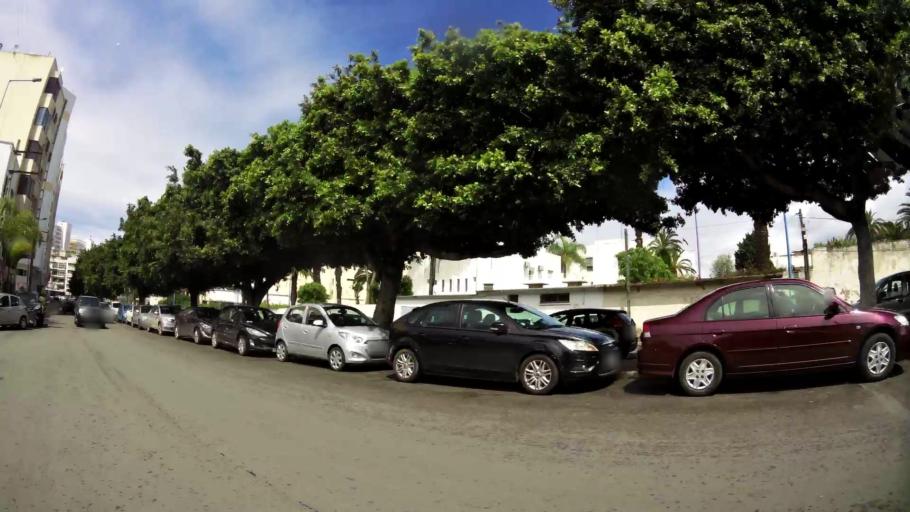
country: MA
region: Grand Casablanca
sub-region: Casablanca
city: Casablanca
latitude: 33.5813
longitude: -7.6218
